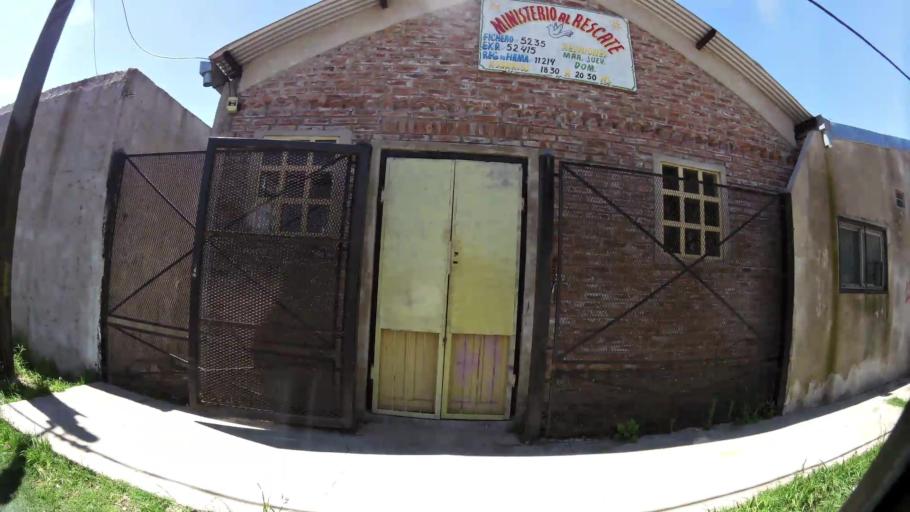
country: AR
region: Buenos Aires
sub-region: Partido de Quilmes
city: Quilmes
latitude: -34.7408
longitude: -58.3081
